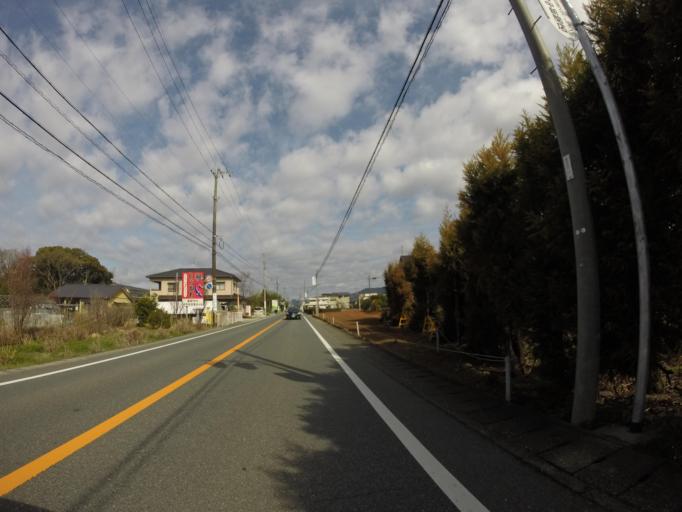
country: JP
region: Shizuoka
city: Hamakita
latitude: 34.7973
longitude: 137.6999
